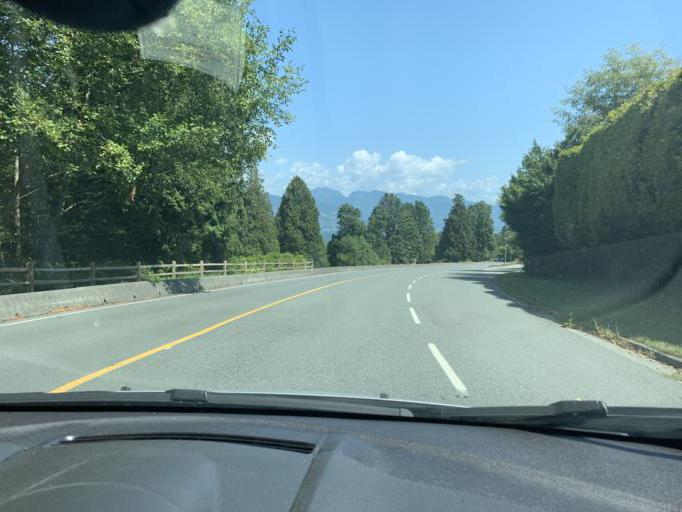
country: CA
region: British Columbia
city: West End
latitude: 49.2767
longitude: -123.2494
